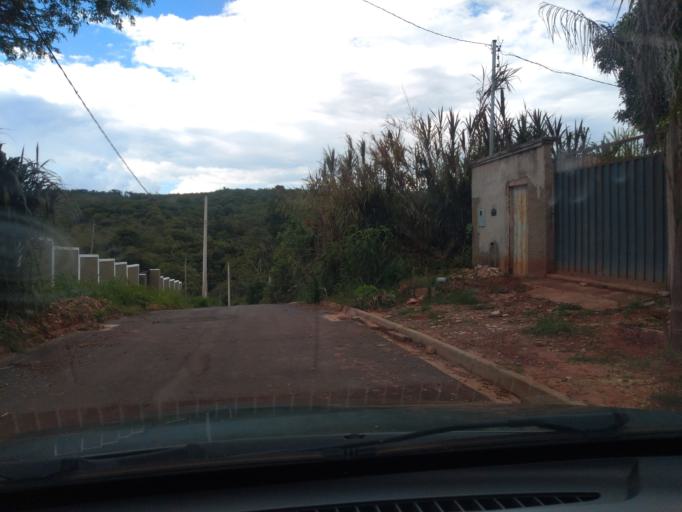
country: BR
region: Minas Gerais
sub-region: Tres Coracoes
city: Tres Coracoes
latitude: -21.6882
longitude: -45.2713
